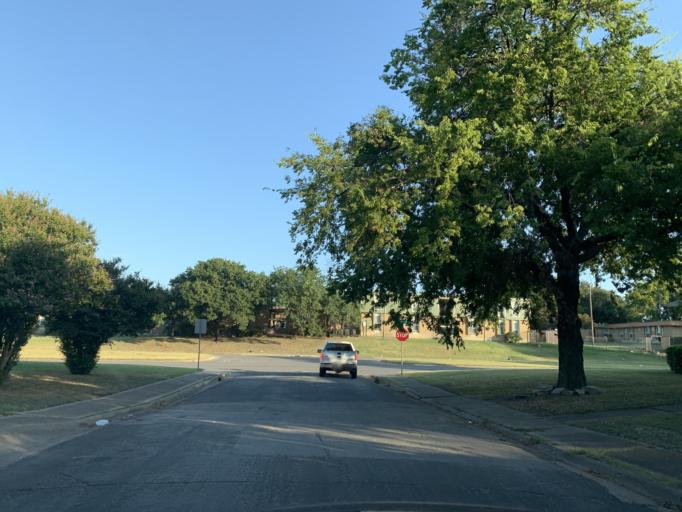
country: US
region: Texas
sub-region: Dallas County
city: Dallas
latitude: 32.7127
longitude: -96.7983
